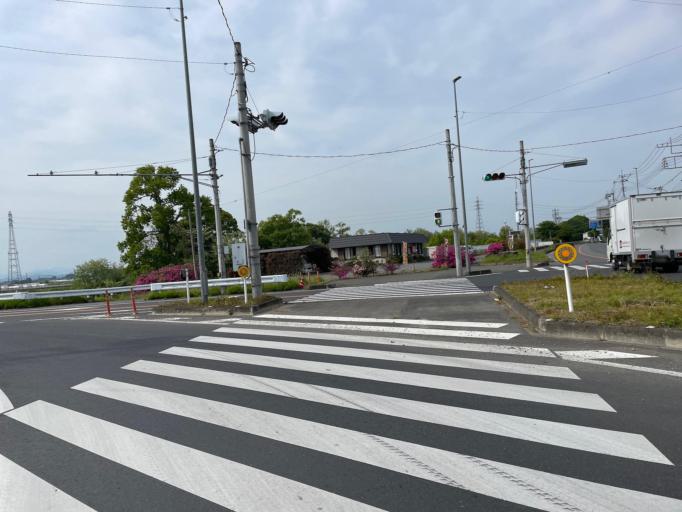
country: JP
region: Tochigi
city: Mibu
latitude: 36.4060
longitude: 139.8041
